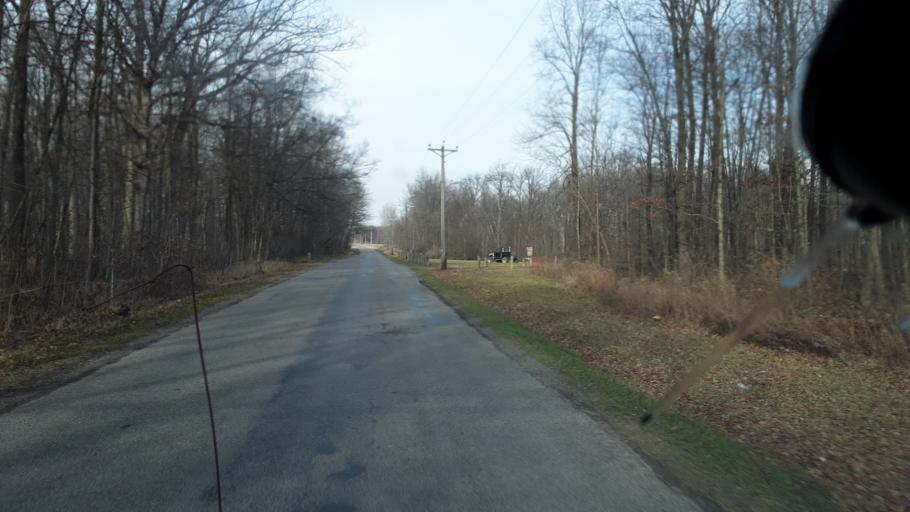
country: US
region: Indiana
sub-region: DeKalb County
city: Butler
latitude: 41.4124
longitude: -84.8894
